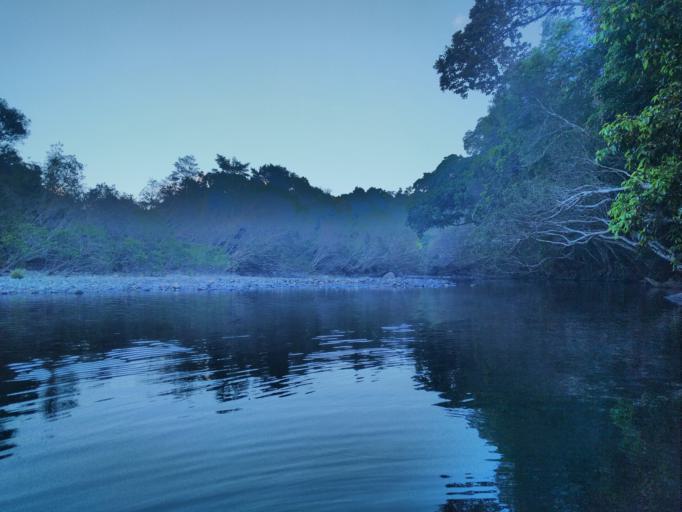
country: AU
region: Queensland
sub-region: Cairns
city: Woree
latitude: -17.2375
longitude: 145.7732
